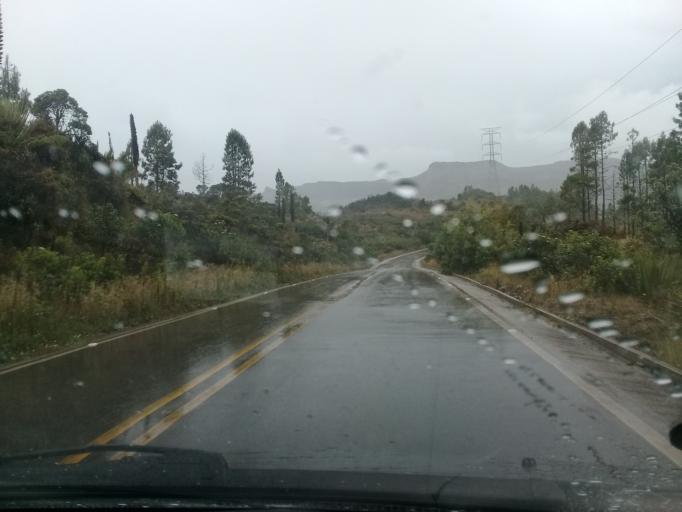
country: CO
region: Cundinamarca
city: Guatavita
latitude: 4.8516
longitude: -73.7755
